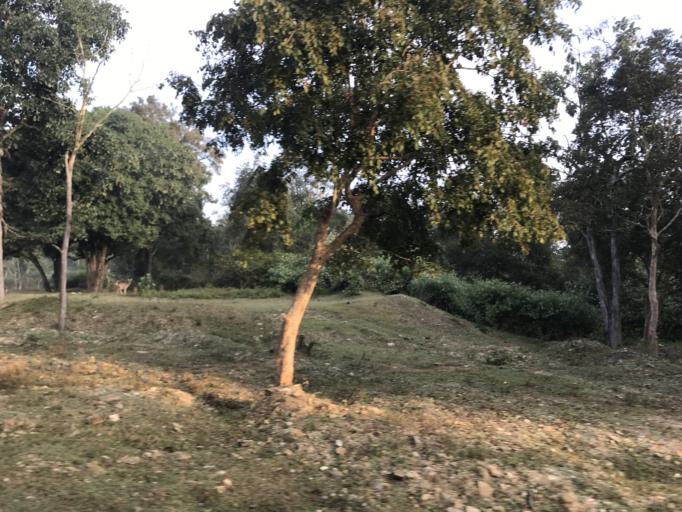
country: IN
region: Karnataka
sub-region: Mysore
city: Heggadadevankote
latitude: 12.0121
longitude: 76.2416
